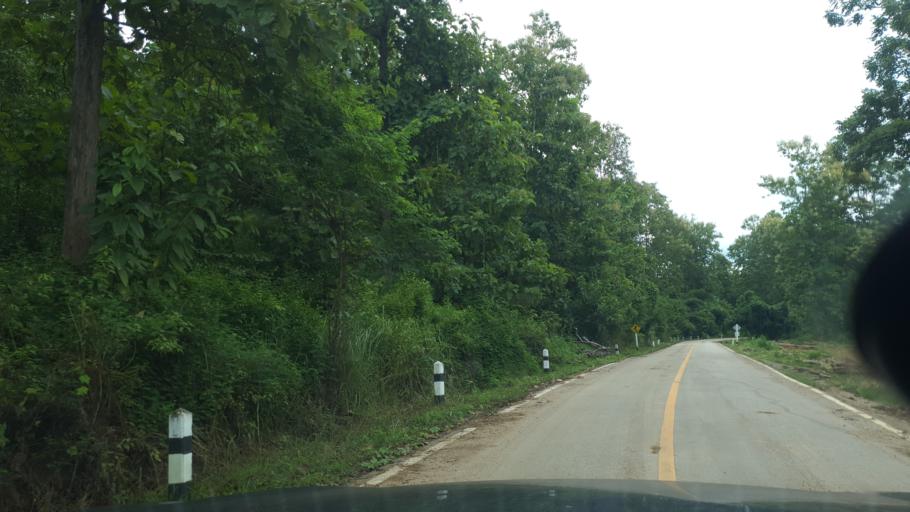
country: TH
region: Lampang
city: Hang Chat
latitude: 18.3752
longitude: 99.2593
